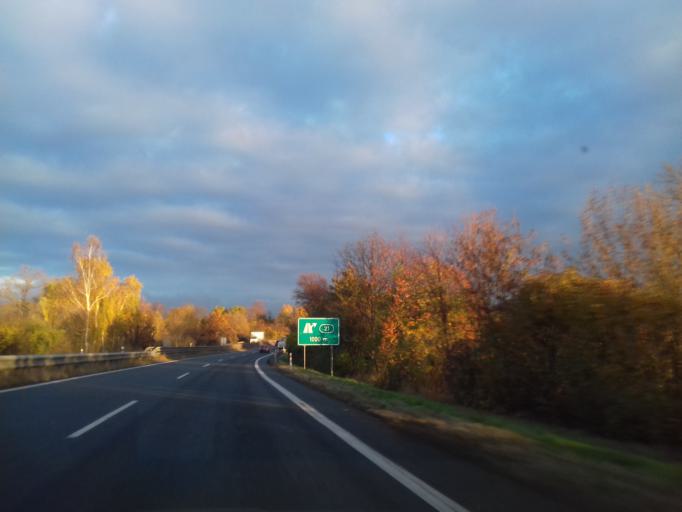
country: CZ
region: Olomoucky
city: Urcice
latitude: 49.4329
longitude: 17.1098
